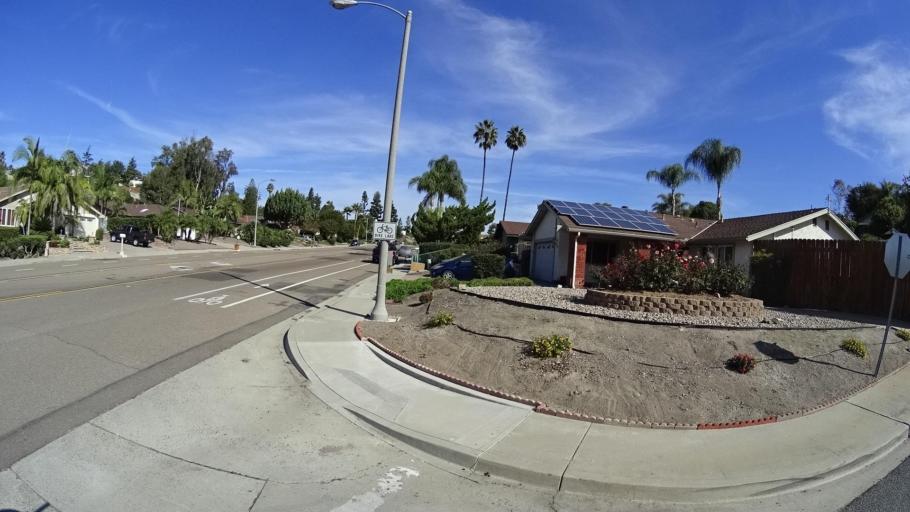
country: US
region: California
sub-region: San Diego County
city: Spring Valley
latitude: 32.7295
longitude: -116.9832
